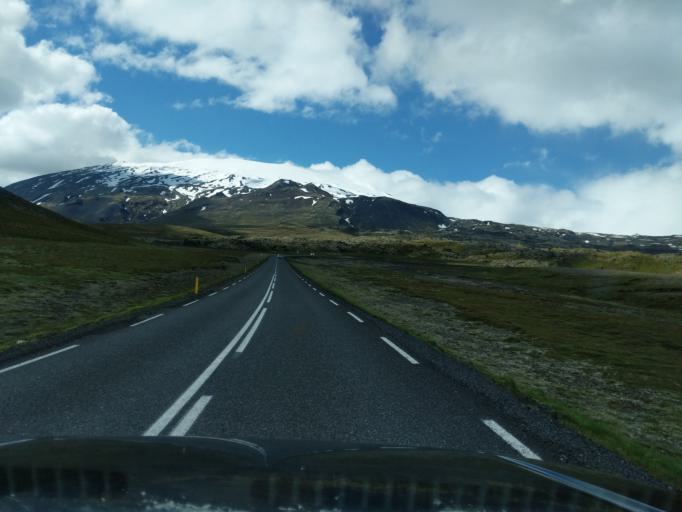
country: IS
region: West
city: Olafsvik
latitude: 64.7597
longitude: -23.6720
